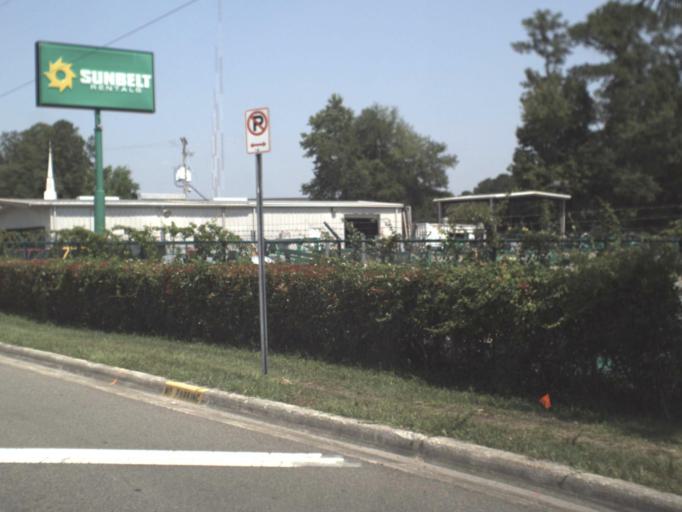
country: US
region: Florida
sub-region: Duval County
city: Jacksonville
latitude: 30.3003
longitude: -81.7653
